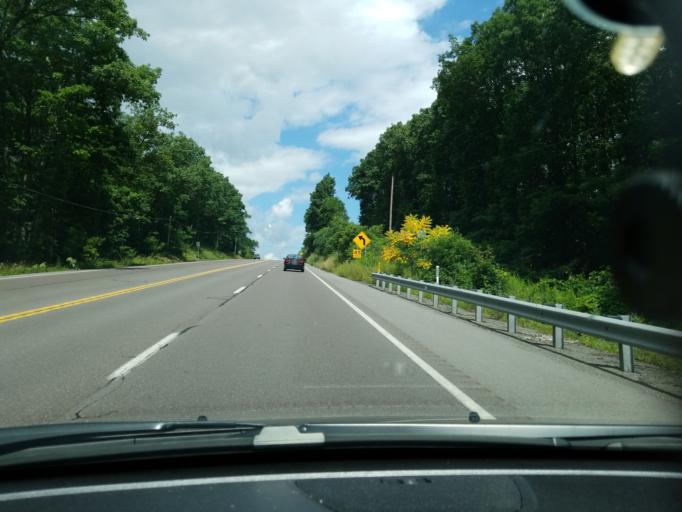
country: US
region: Pennsylvania
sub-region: Northumberland County
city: Elysburg
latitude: 40.8464
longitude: -76.5223
